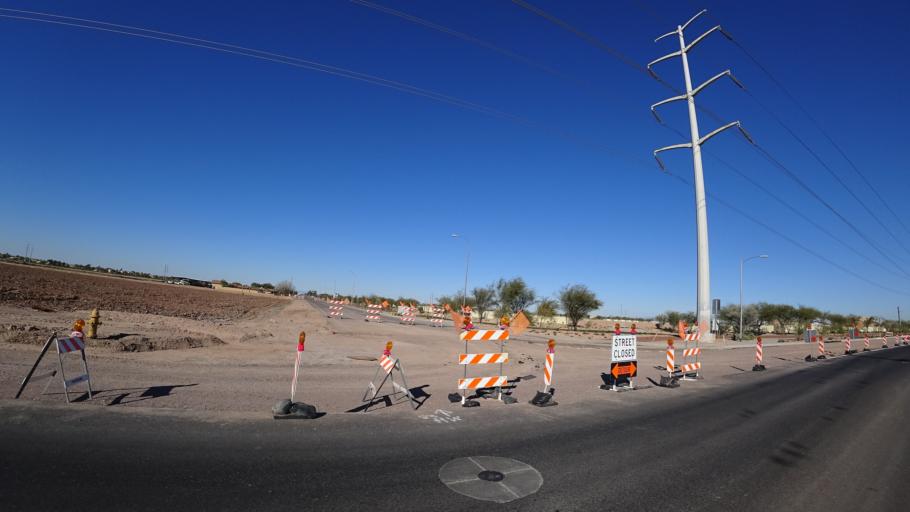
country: US
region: Arizona
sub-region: Maricopa County
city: Tolleson
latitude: 33.4084
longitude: -112.2381
